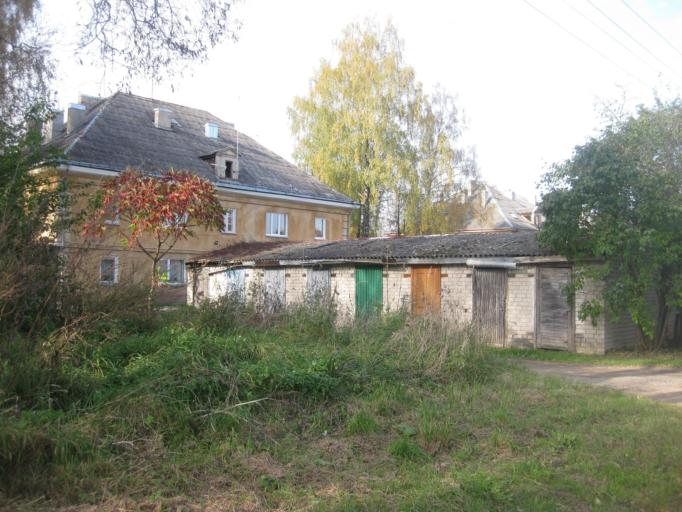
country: LT
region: Kauno apskritis
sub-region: Kaunas
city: Aleksotas
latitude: 54.8895
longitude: 23.8869
